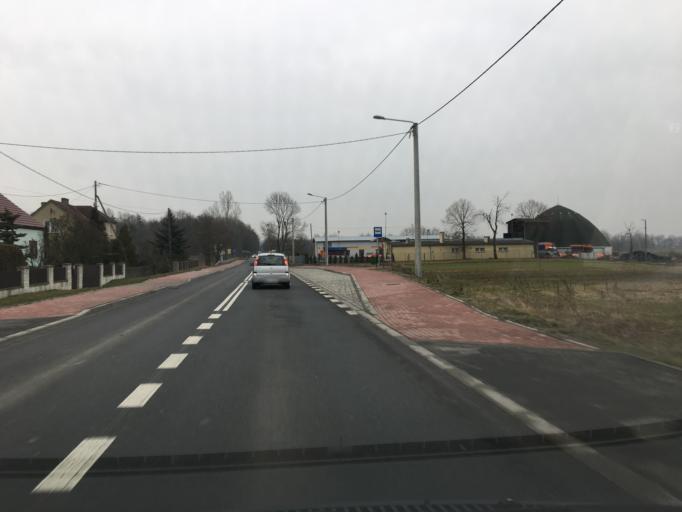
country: PL
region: Opole Voivodeship
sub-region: Powiat kedzierzynsko-kozielski
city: Bierawa
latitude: 50.3068
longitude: 18.2288
